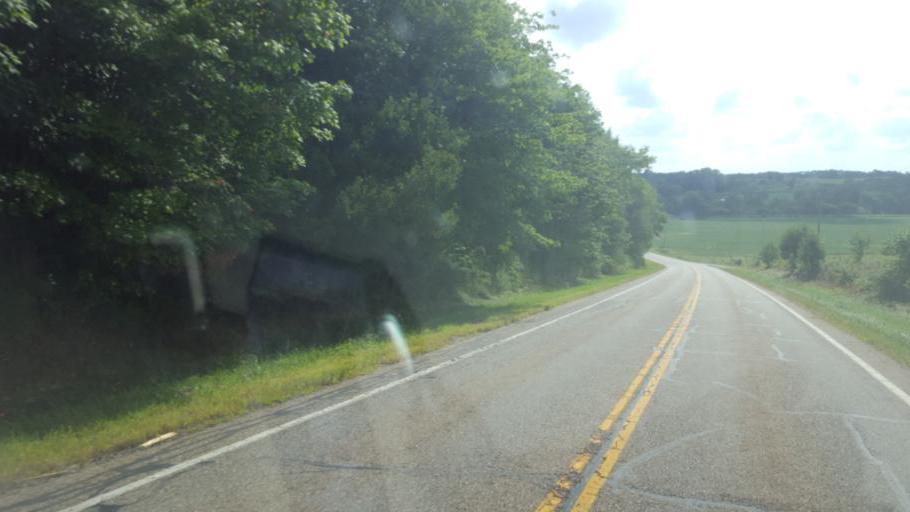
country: US
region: Ohio
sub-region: Stark County
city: Minerva
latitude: 40.7984
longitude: -81.0764
